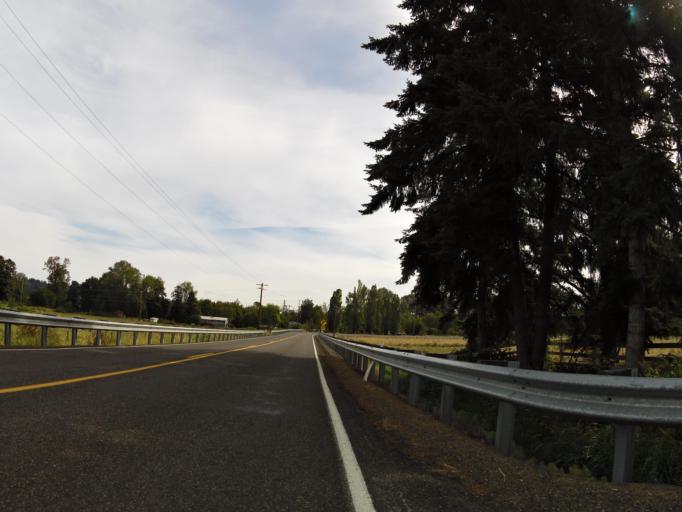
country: US
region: Washington
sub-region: Lewis County
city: Chehalis
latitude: 46.6413
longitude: -122.9749
